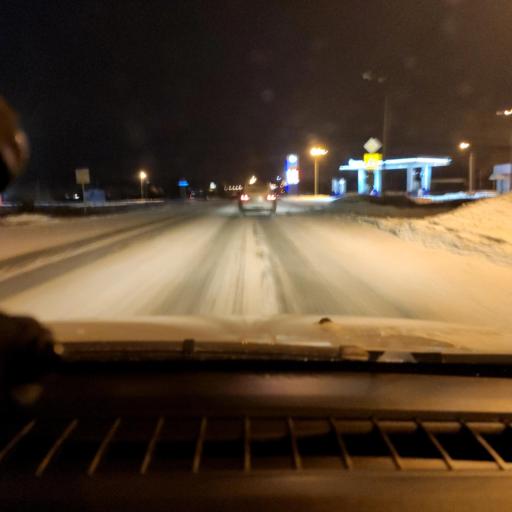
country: RU
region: Samara
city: Krotovka
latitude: 53.2961
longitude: 51.1800
